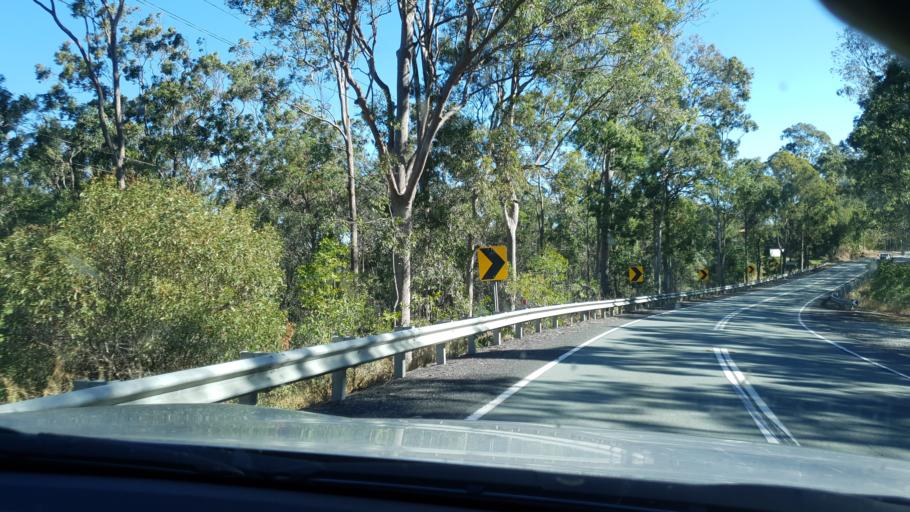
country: AU
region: Queensland
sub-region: Moreton Bay
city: Ferny Hills
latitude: -27.3309
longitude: 152.9292
